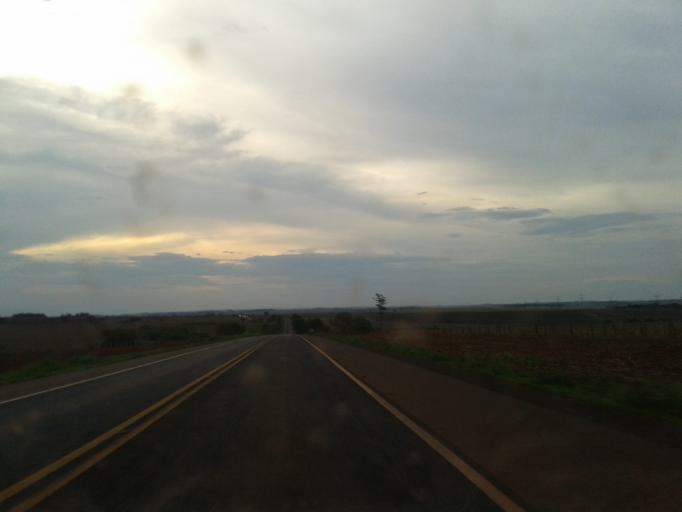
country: BR
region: Goias
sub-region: Santa Helena De Goias
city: Santa Helena de Goias
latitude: -17.8992
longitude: -50.6459
